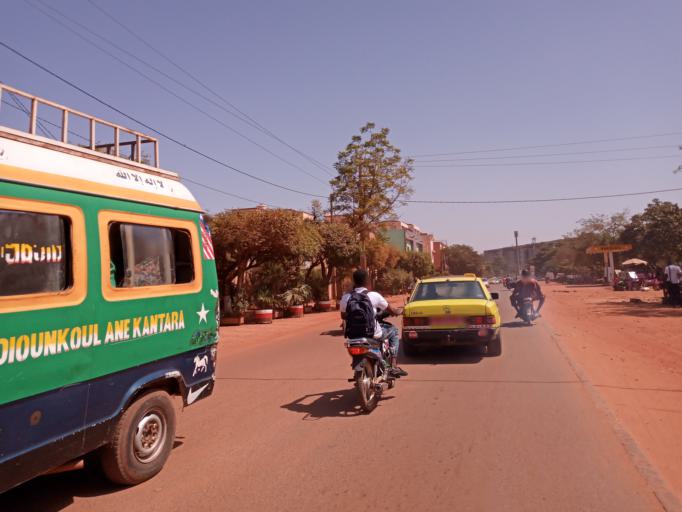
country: ML
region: Bamako
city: Bamako
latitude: 12.6140
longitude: -7.9958
